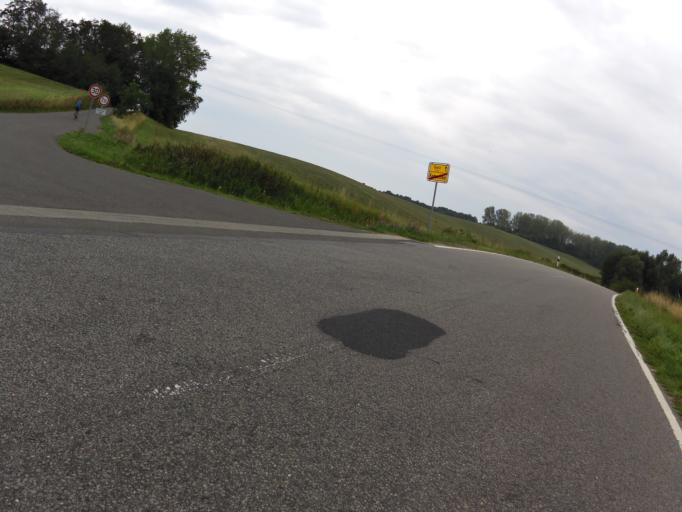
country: PL
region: West Pomeranian Voivodeship
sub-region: Swinoujscie
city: Swinoujscie
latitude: 53.8792
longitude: 14.2038
